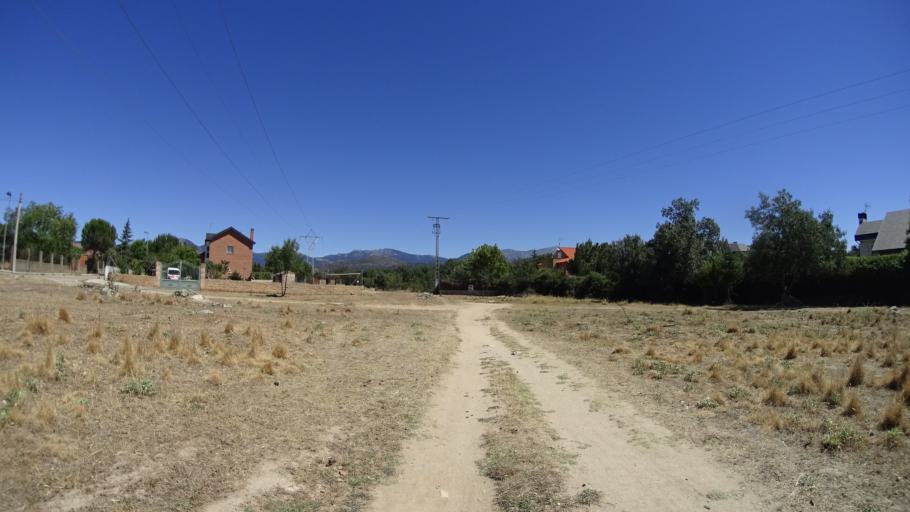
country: ES
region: Madrid
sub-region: Provincia de Madrid
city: Alpedrete
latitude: 40.6592
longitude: -4.0480
